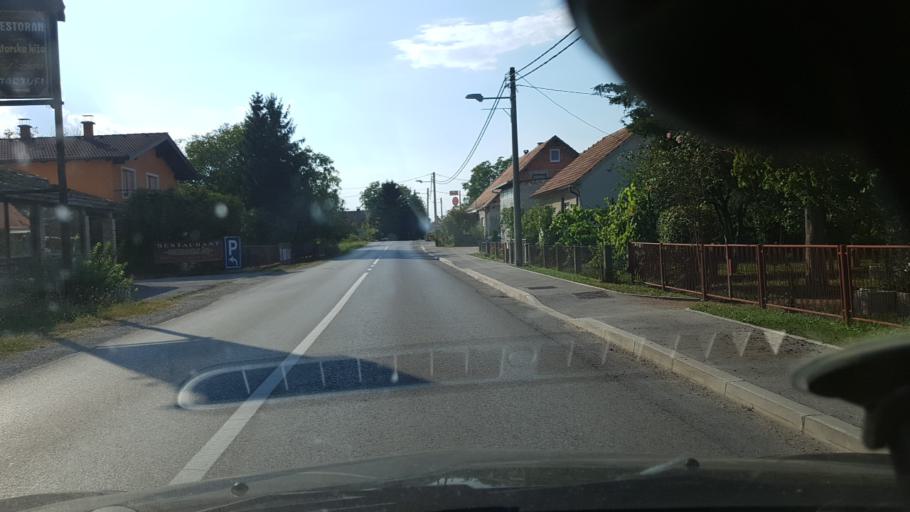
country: HR
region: Zagrebacka
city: Bregana
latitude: 45.8885
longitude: 15.6932
